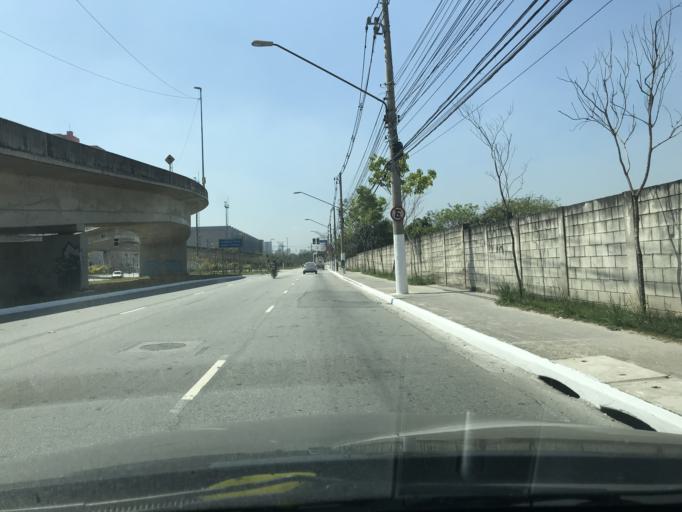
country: BR
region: Sao Paulo
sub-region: Taboao Da Serra
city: Taboao da Serra
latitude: -23.6650
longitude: -46.7265
